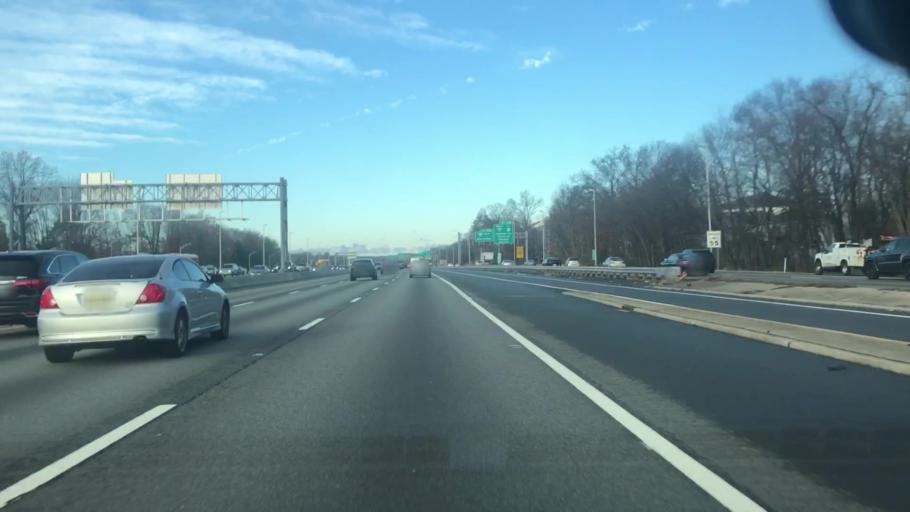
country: US
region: New Jersey
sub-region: Morris County
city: Parsippany
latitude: 40.8618
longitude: -74.4033
